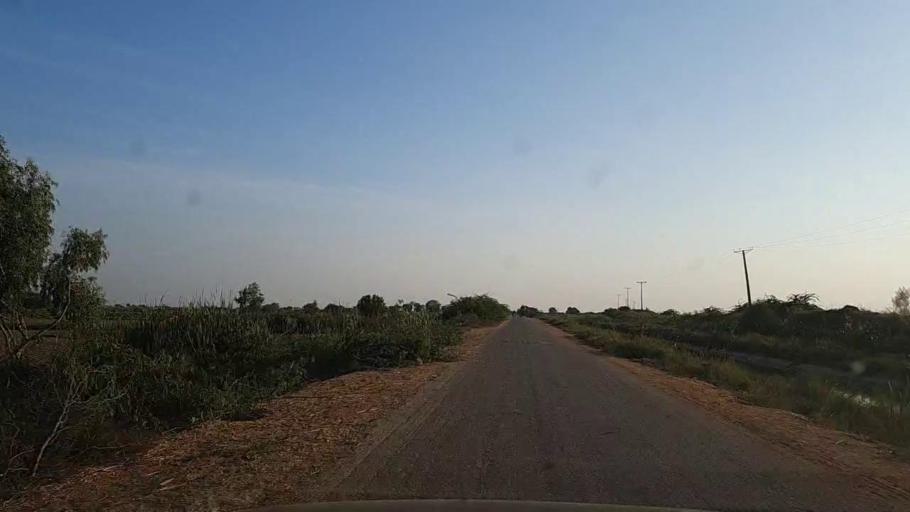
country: PK
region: Sindh
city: Thatta
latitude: 24.6393
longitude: 67.9125
